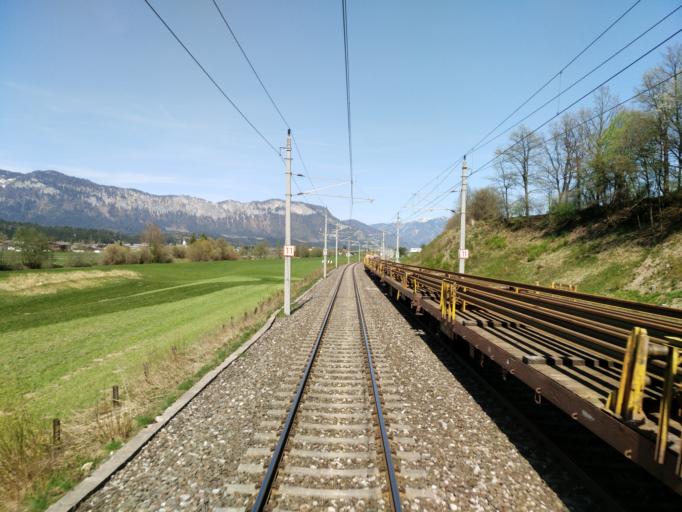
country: AT
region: Tyrol
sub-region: Politischer Bezirk Kitzbuhel
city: Oberndorf in Tirol
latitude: 47.4881
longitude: 12.3831
